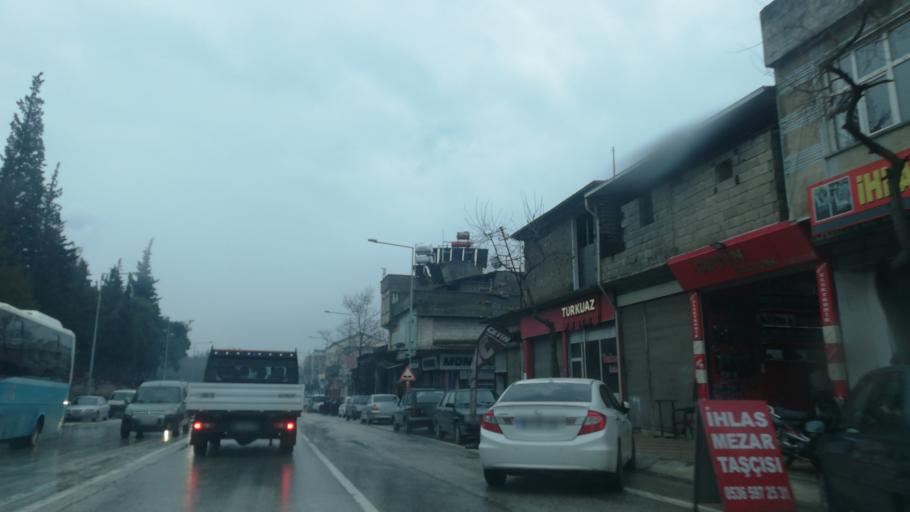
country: TR
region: Kahramanmaras
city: Kahramanmaras
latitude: 37.5751
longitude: 36.9366
